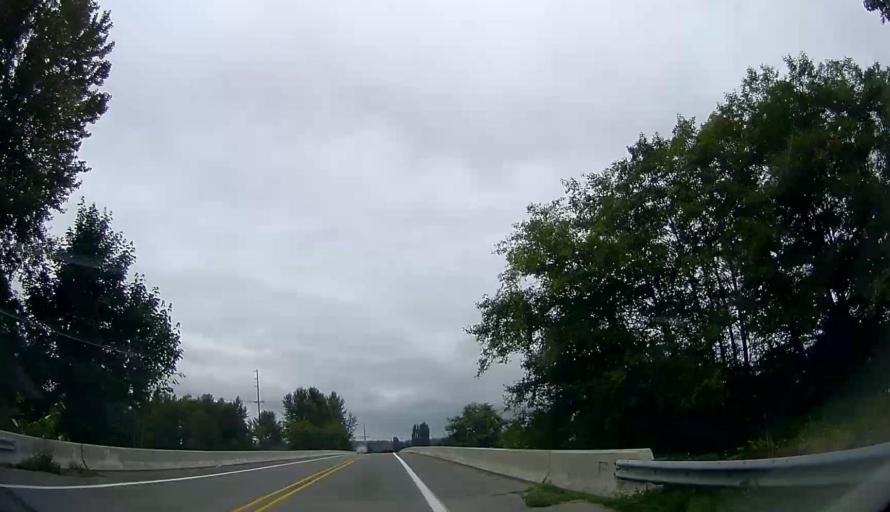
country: US
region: Washington
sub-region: Snohomish County
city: Stanwood
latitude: 48.2101
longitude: -122.3366
